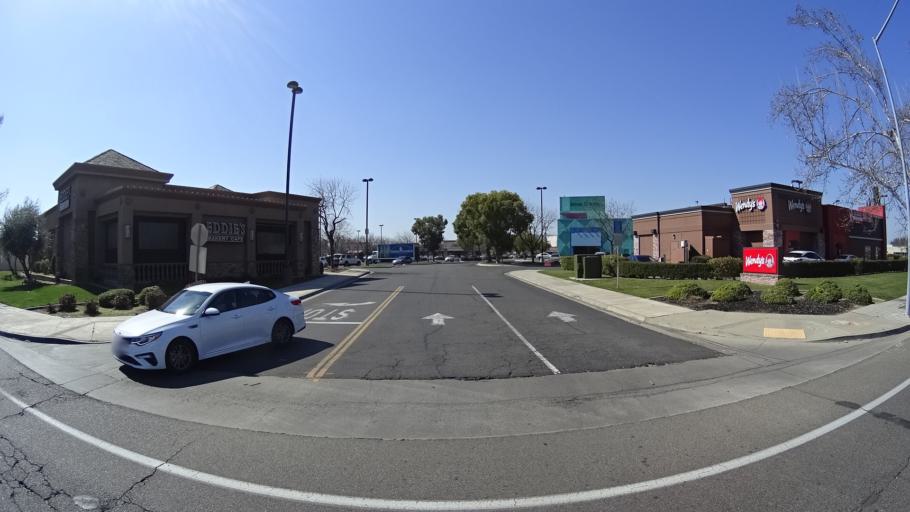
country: US
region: California
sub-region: Fresno County
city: Clovis
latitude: 36.8391
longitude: -119.7546
